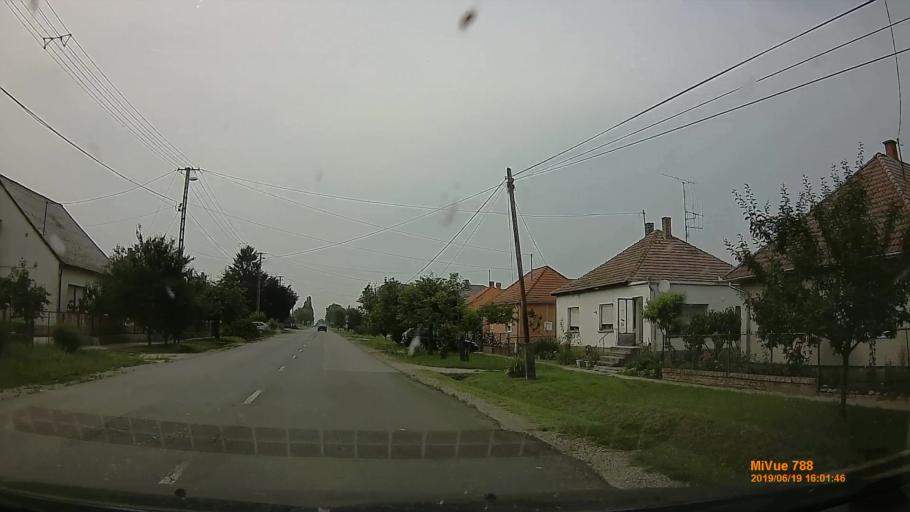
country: HU
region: Baranya
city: Szigetvar
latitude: 46.0526
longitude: 17.7824
